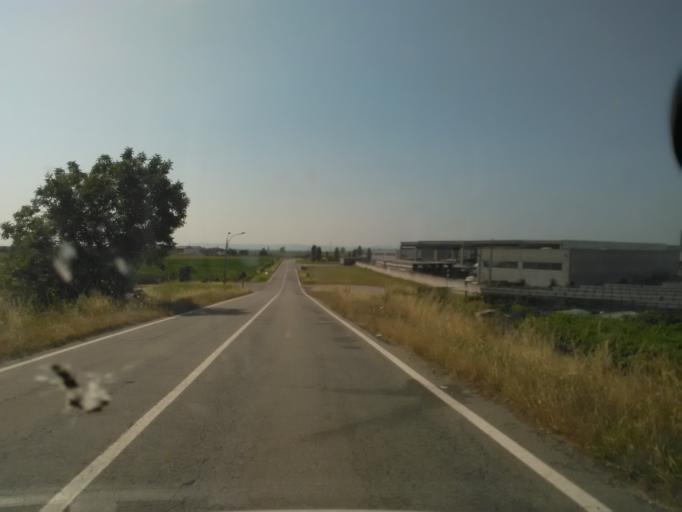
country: IT
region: Piedmont
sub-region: Provincia di Vercelli
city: Bianze
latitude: 45.3052
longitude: 8.1108
